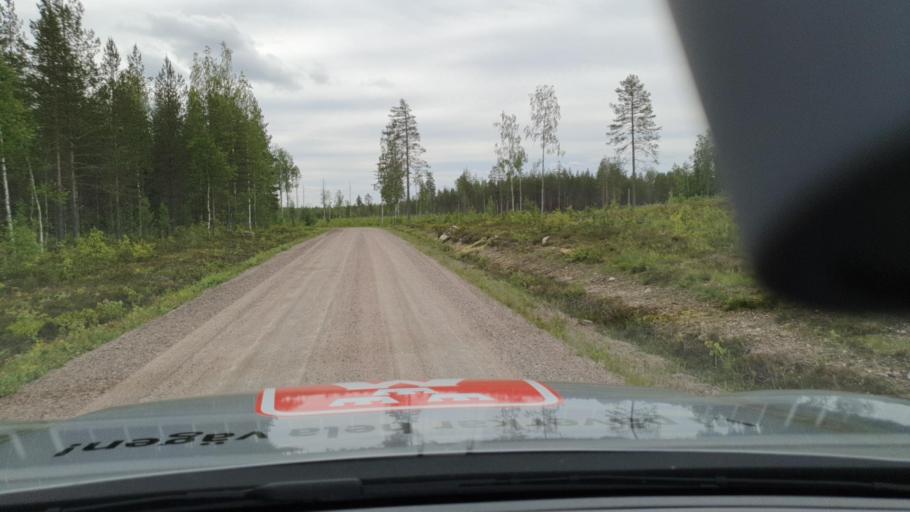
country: SE
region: Norrbotten
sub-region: Kalix Kommun
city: Kalix
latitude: 66.0339
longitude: 23.3869
